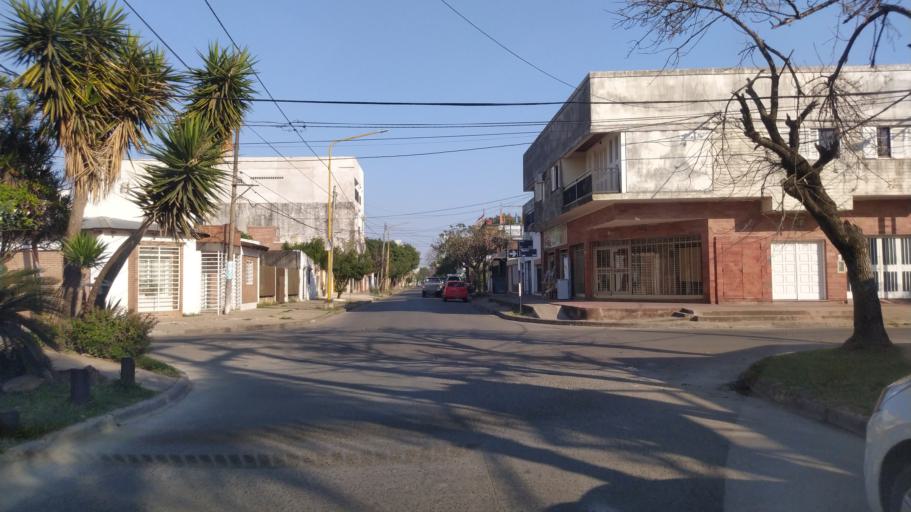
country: AR
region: Corrientes
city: Corrientes
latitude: -27.4741
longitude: -58.8160
